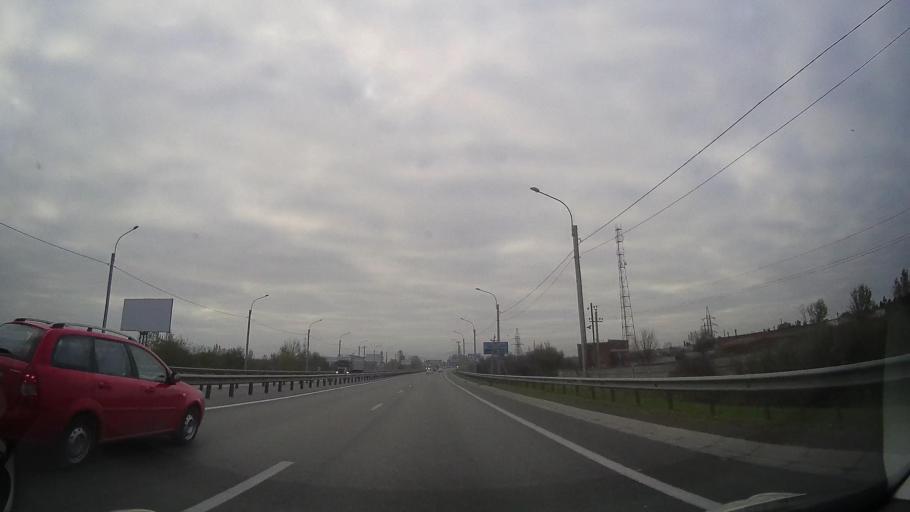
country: RU
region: Rostov
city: Bataysk
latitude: 47.1598
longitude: 39.7649
